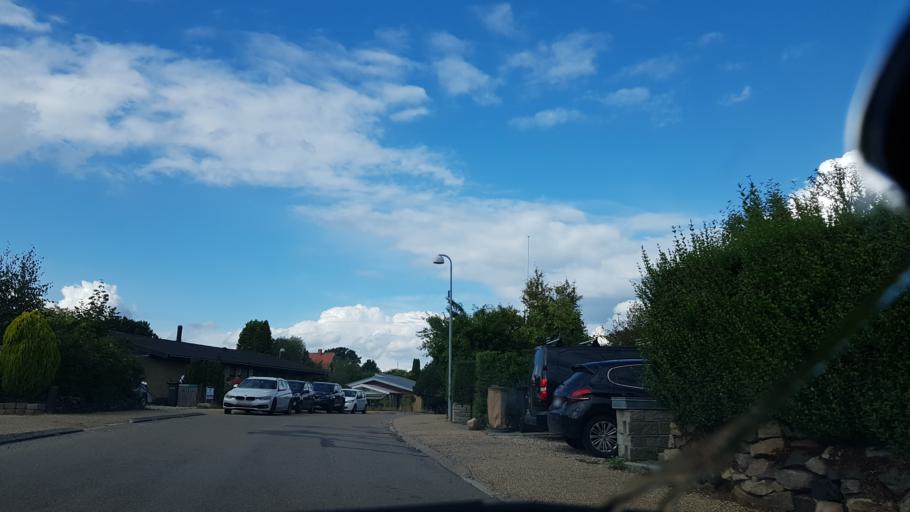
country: DK
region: Capital Region
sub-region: Fredensborg Kommune
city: Humlebaek
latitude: 55.9900
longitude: 12.5384
